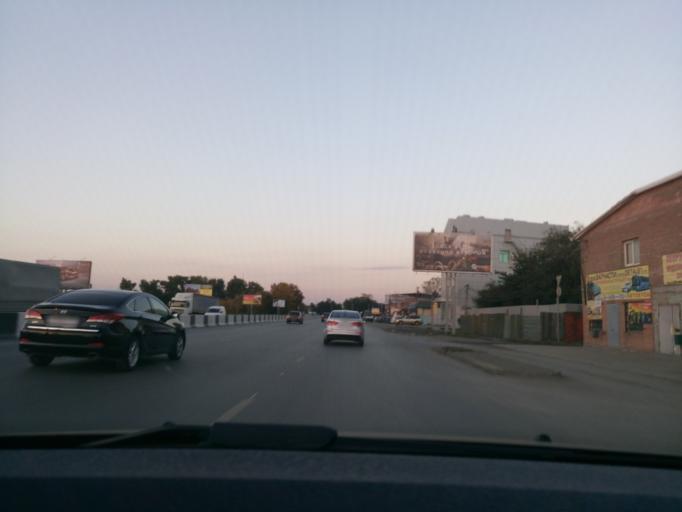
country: RU
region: Rostov
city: Severnyy
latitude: 47.2577
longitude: 39.6185
